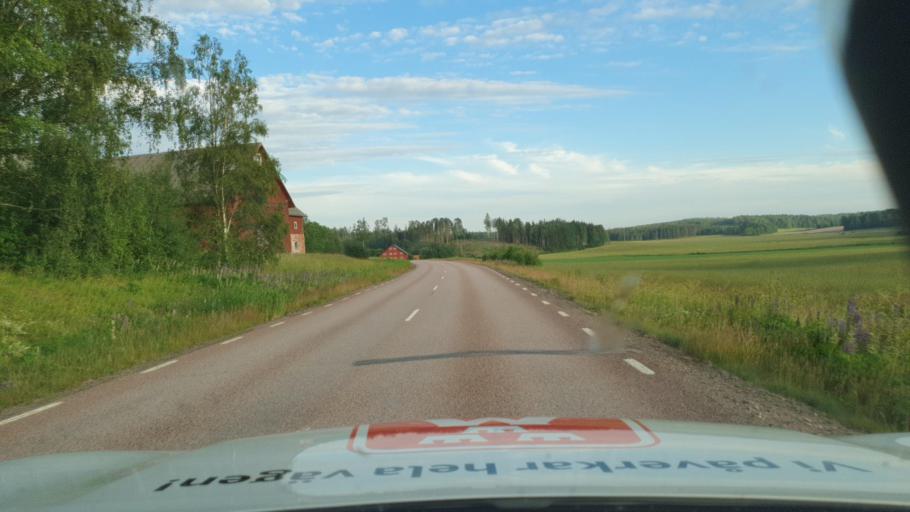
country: SE
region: Vaermland
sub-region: Karlstads Kommun
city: Molkom
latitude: 59.4723
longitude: 13.8091
